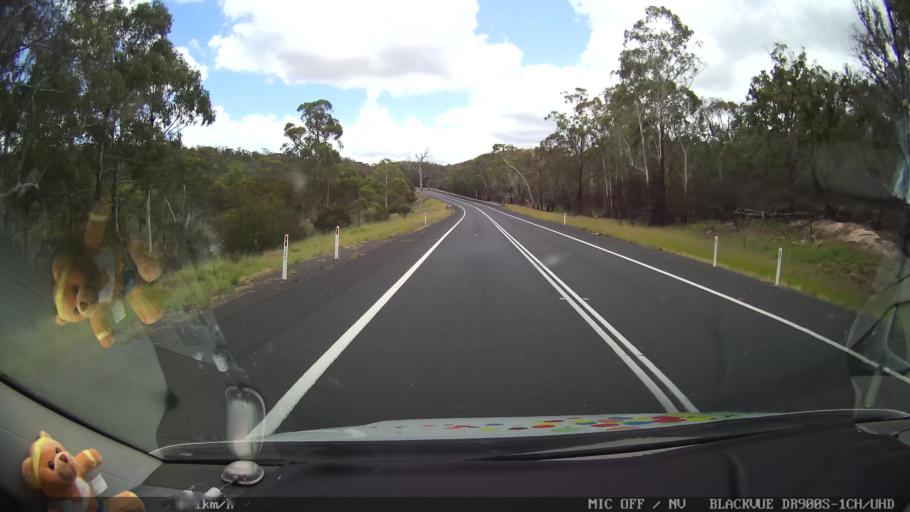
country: AU
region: New South Wales
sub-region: Glen Innes Severn
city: Glen Innes
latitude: -29.3546
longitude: 151.8974
